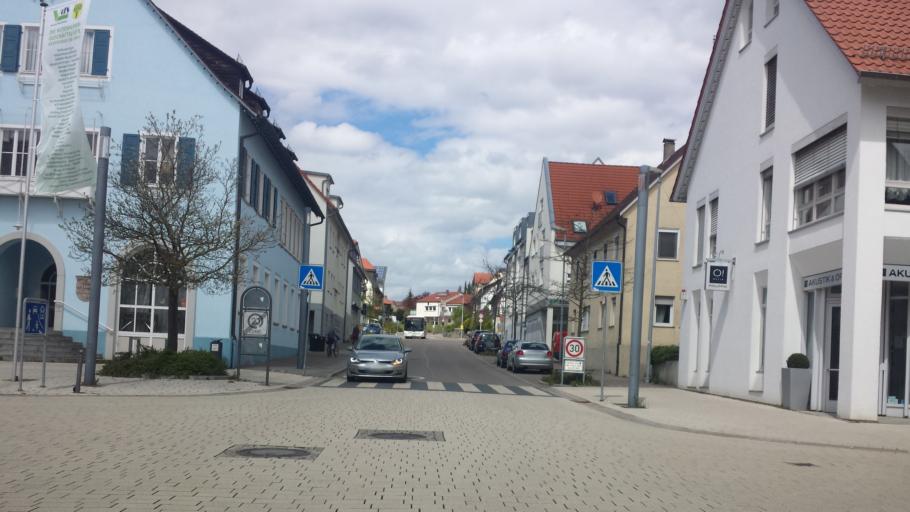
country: DE
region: Baden-Wuerttemberg
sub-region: Regierungsbezirk Stuttgart
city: Rutesheim
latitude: 48.8090
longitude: 8.9454
